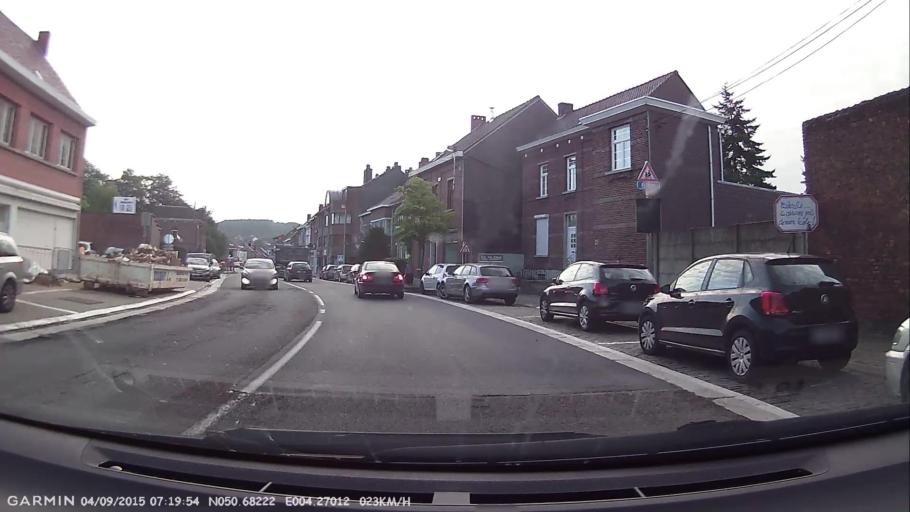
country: BE
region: Wallonia
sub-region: Province du Brabant Wallon
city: Braine-le-Chateau
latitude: 50.6822
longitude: 4.2702
